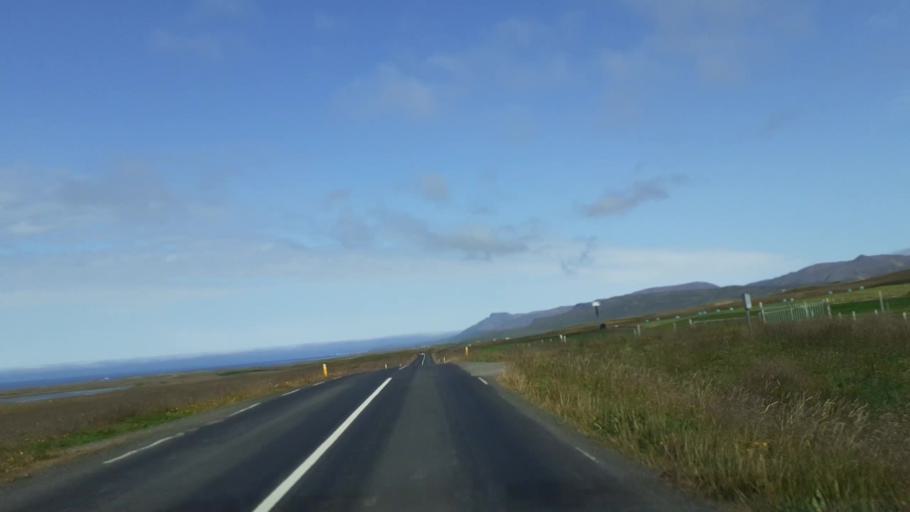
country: IS
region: Northwest
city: Saudarkrokur
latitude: 65.6917
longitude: -20.2374
